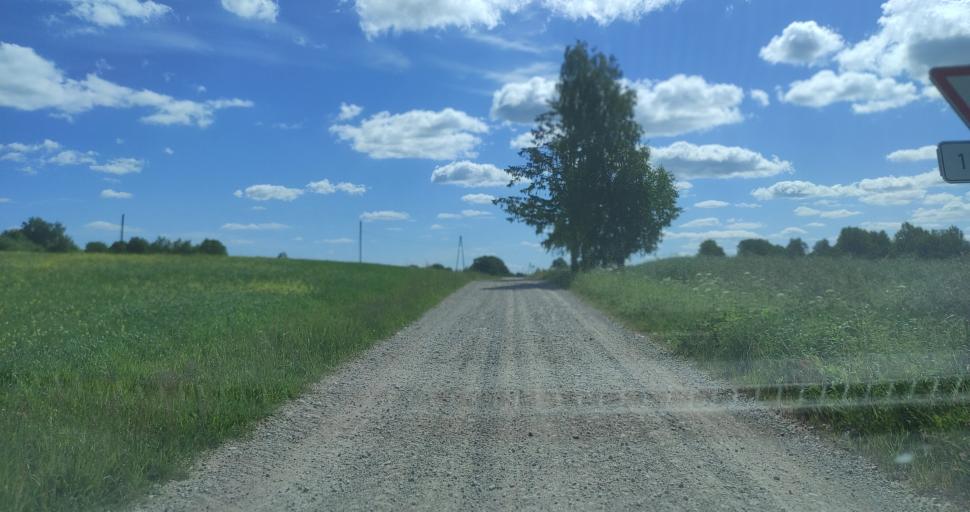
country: LV
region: Alsunga
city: Alsunga
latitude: 56.8995
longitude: 21.7057
